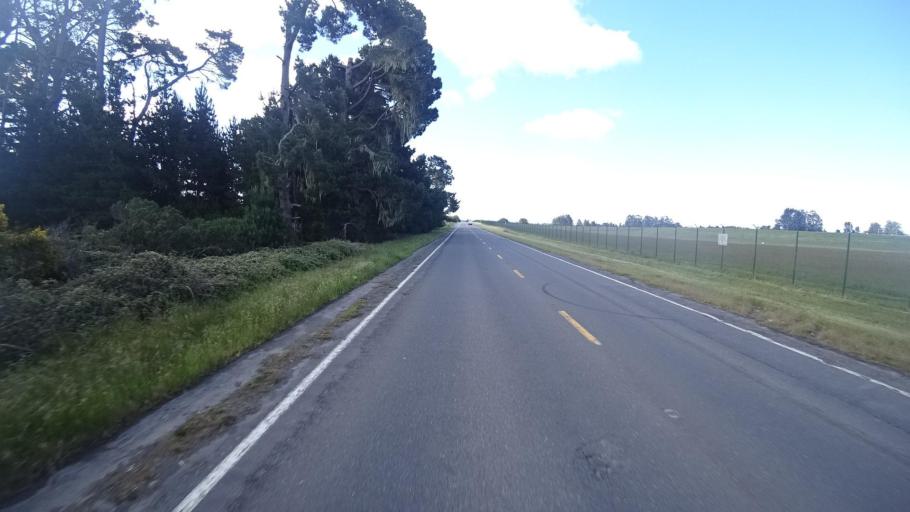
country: US
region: California
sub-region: Humboldt County
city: McKinleyville
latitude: 40.9725
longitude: -124.1006
